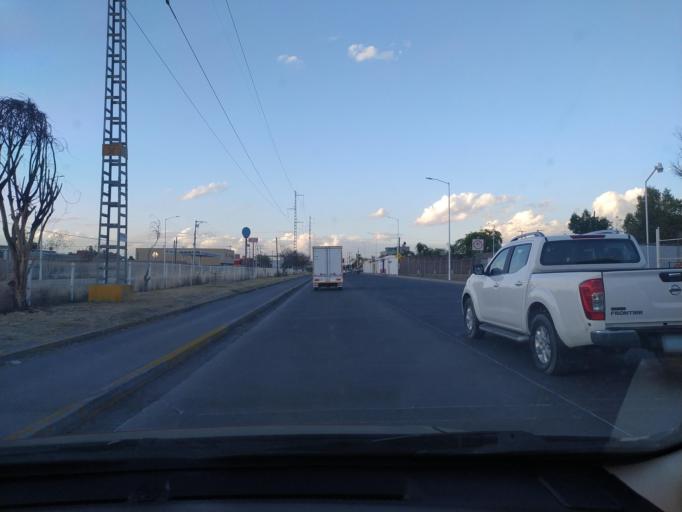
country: LA
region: Oudomxai
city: Muang La
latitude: 21.0152
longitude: 101.8697
